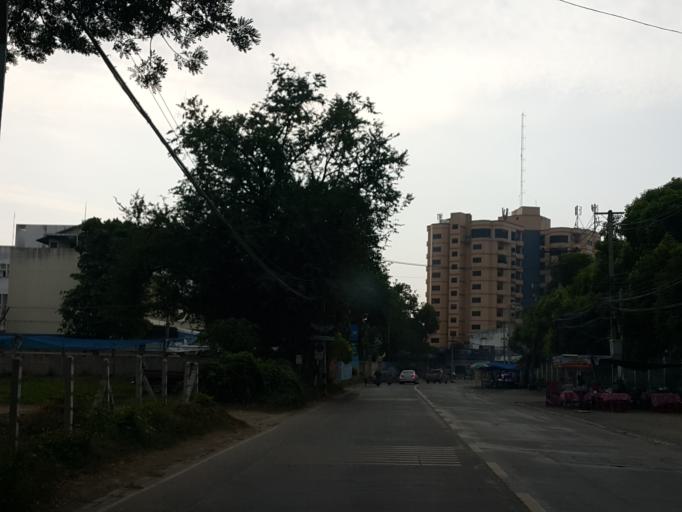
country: TH
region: Chiang Mai
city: Chiang Mai
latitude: 18.7952
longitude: 99.0174
